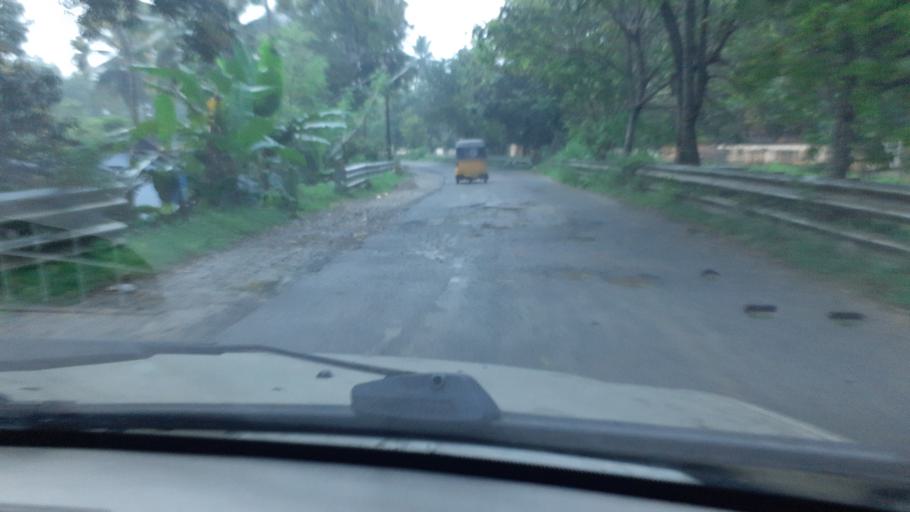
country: IN
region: Tamil Nadu
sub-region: Kanniyakumari
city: Padmanabhapuram
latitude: 8.3620
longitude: 77.3153
